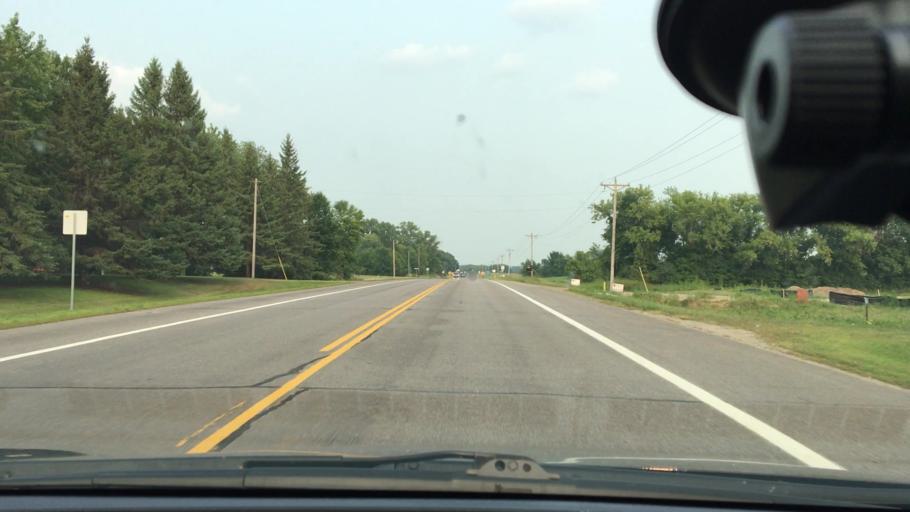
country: US
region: Minnesota
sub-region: Wright County
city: Albertville
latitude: 45.2896
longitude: -93.6728
